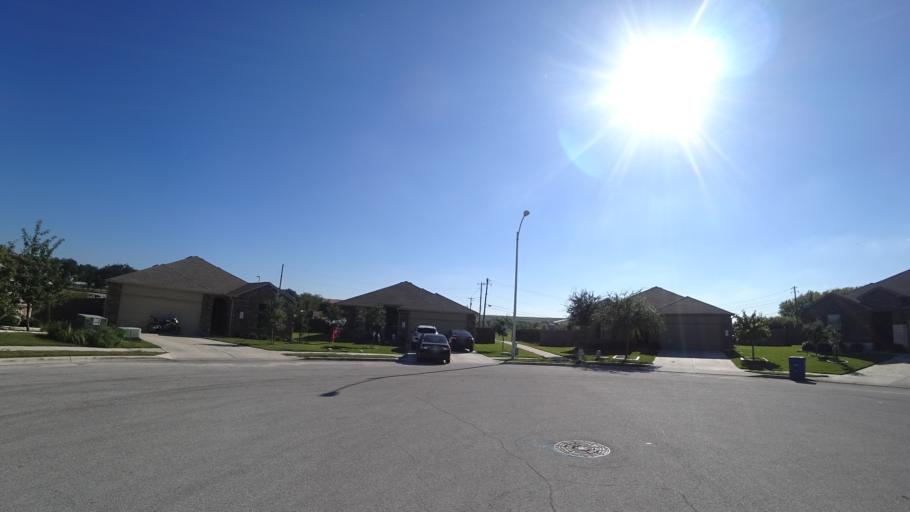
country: US
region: Texas
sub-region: Travis County
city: Manor
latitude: 30.3533
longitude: -97.6184
